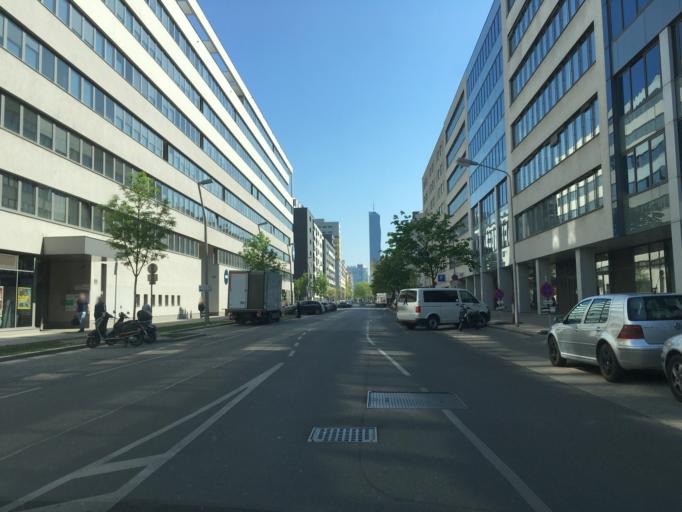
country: AT
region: Vienna
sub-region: Wien Stadt
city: Vienna
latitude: 48.2237
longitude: 16.3975
